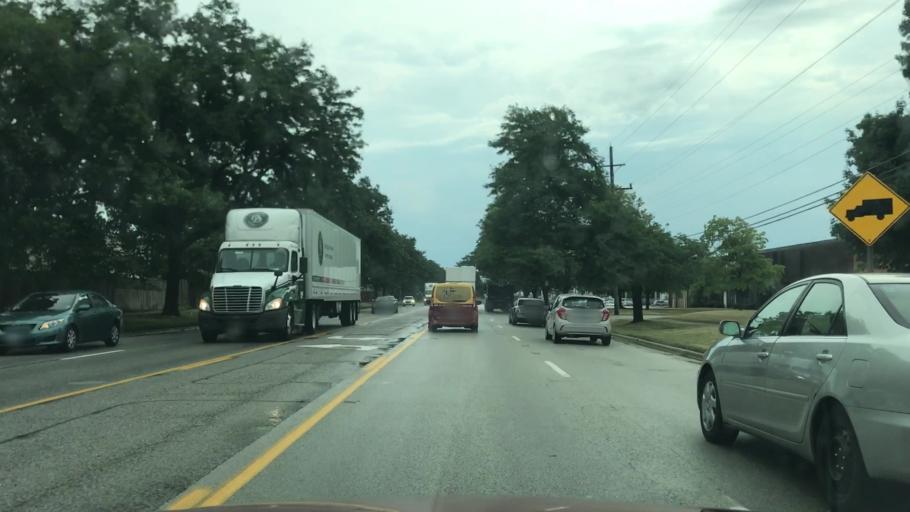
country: US
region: Illinois
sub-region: Cook County
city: Mount Prospect
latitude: 42.0228
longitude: -87.9301
